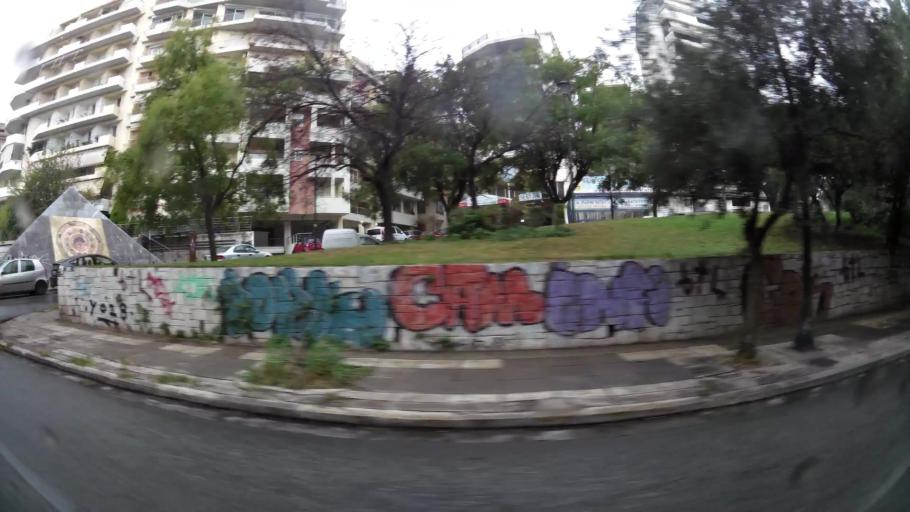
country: GR
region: Attica
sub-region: Nomarchia Athinas
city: Dhafni
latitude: 37.9614
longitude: 23.7364
